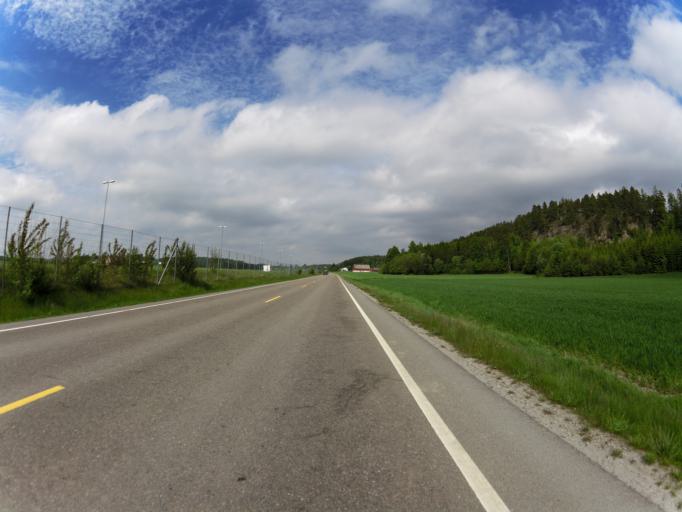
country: NO
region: Ostfold
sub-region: Rade
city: Karlshus
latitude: 59.3307
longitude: 10.9378
